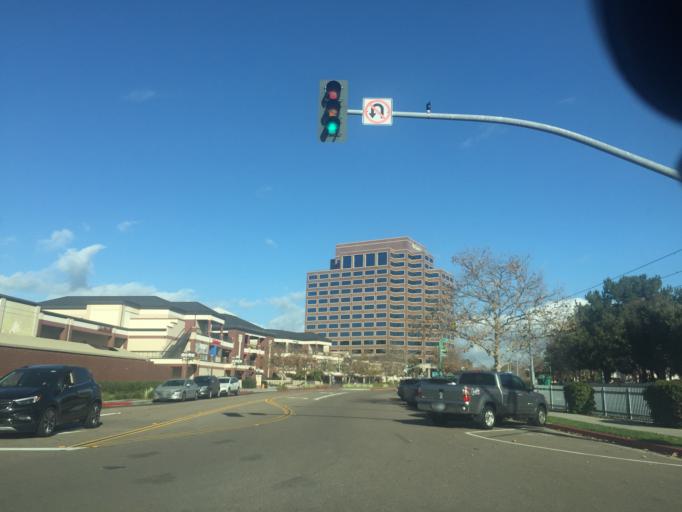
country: US
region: California
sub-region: San Diego County
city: San Diego
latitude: 32.7698
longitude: -117.1594
